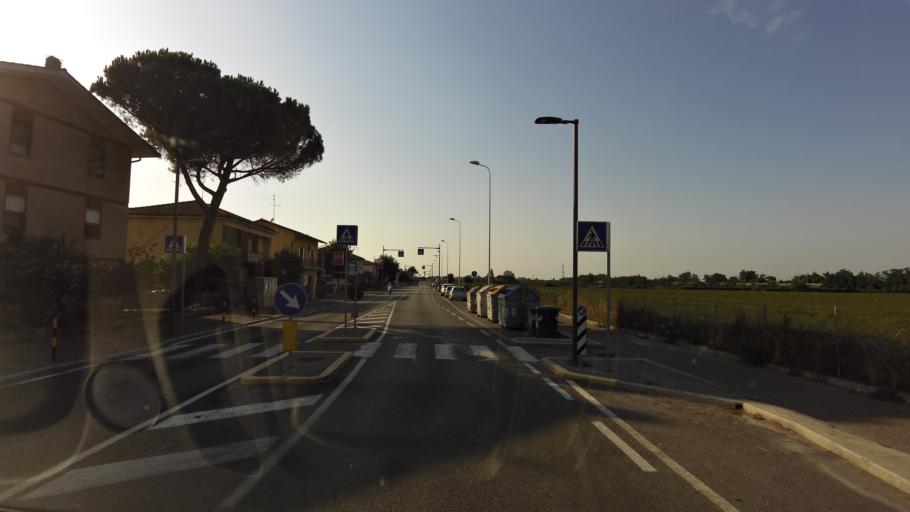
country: IT
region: Emilia-Romagna
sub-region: Provincia di Ravenna
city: Classe
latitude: 44.3908
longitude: 12.2212
